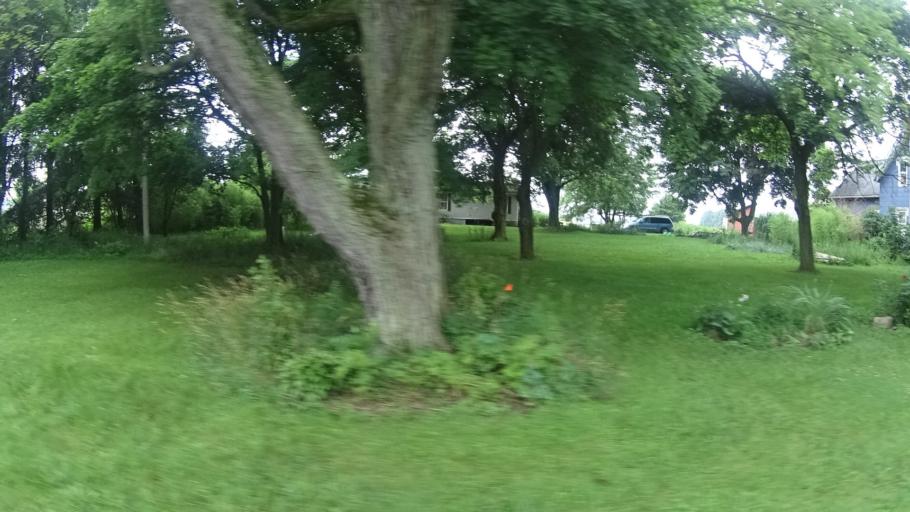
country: US
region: Ohio
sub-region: Huron County
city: Wakeman
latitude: 41.2841
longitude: -82.4555
